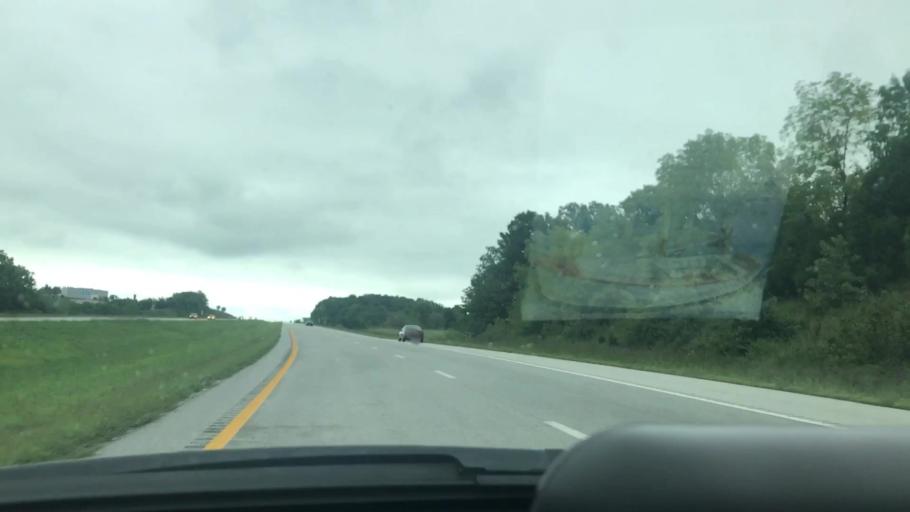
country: US
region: Missouri
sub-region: Greene County
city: Strafford
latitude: 37.2927
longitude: -93.1804
